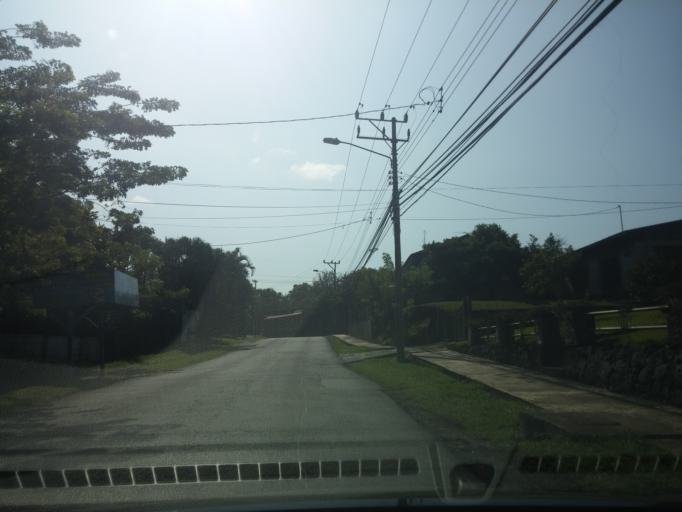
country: CR
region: Heredia
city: Mercedes
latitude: 10.0136
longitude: -84.1468
